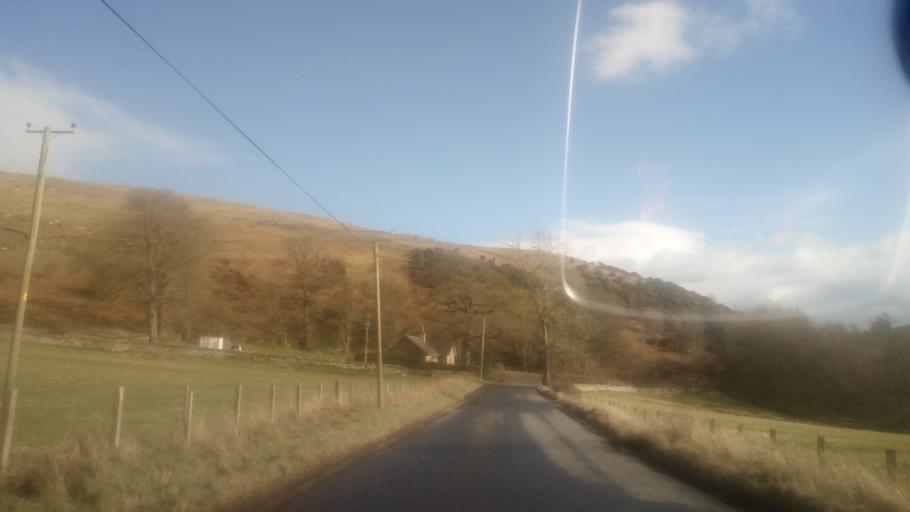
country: GB
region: Scotland
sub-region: The Scottish Borders
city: Hawick
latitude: 55.4166
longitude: -2.8530
